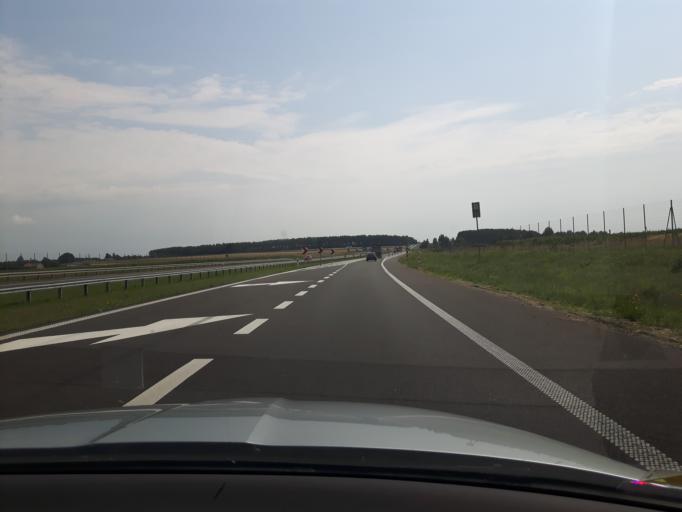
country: PL
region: Masovian Voivodeship
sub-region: Powiat mlawski
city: Wieczfnia Koscielna
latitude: 53.2180
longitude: 20.4269
